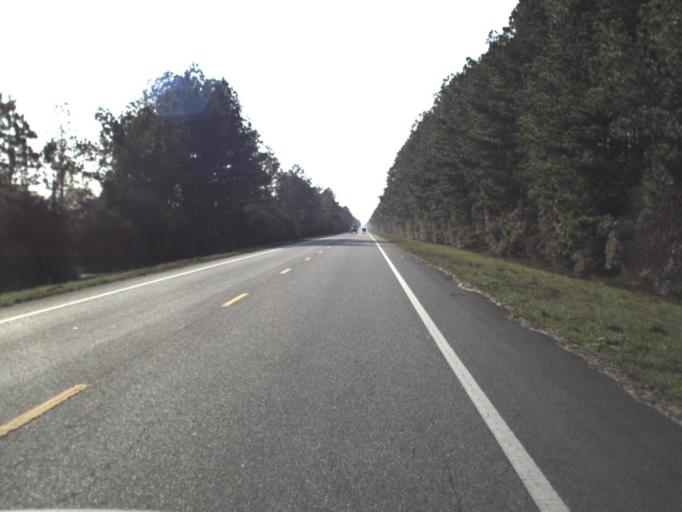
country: US
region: Florida
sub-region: Bay County
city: Lynn Haven
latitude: 30.4394
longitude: -85.7498
